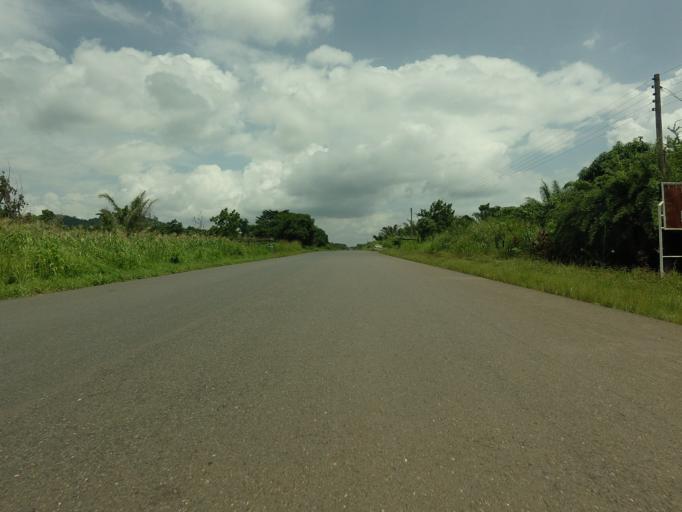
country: GH
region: Volta
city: Ho
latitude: 6.5118
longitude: 0.2160
